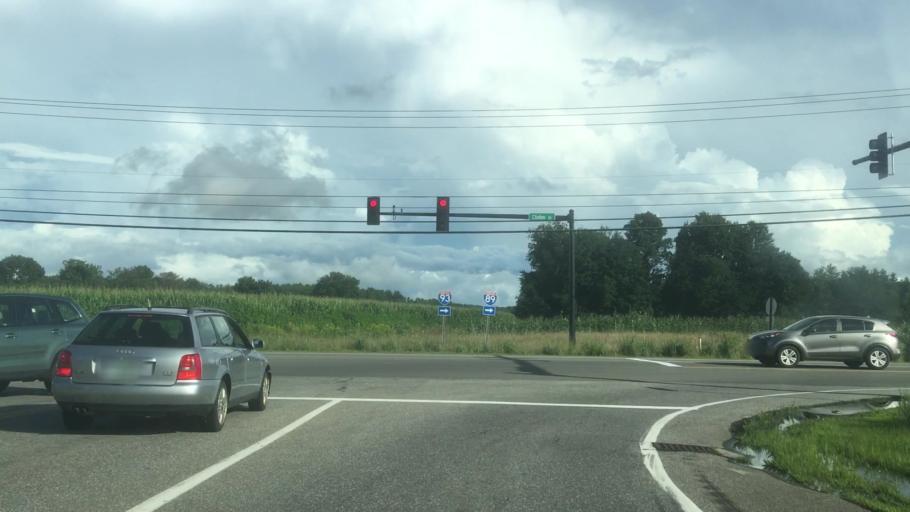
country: US
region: New Hampshire
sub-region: Merrimack County
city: Concord
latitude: 43.1880
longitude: -71.5552
